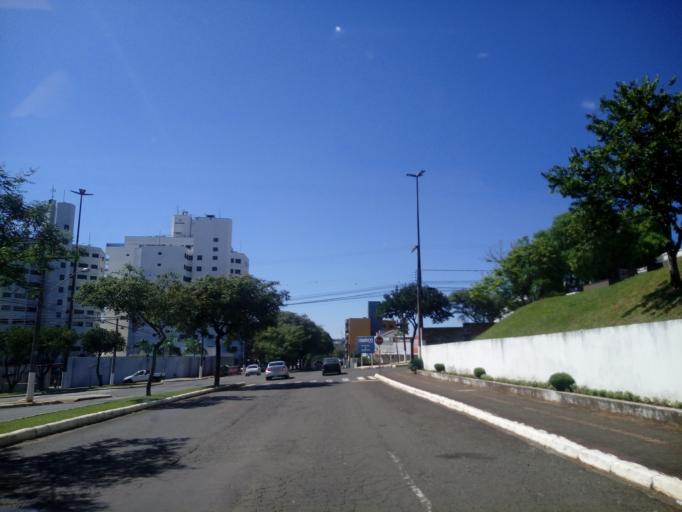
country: BR
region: Santa Catarina
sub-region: Chapeco
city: Chapeco
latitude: -27.1118
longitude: -52.6129
